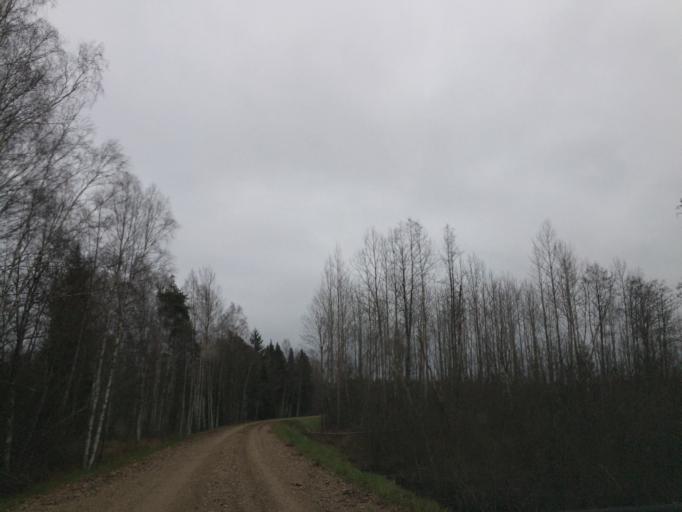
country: LV
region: Burtnieki
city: Matisi
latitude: 57.5464
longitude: 25.1530
